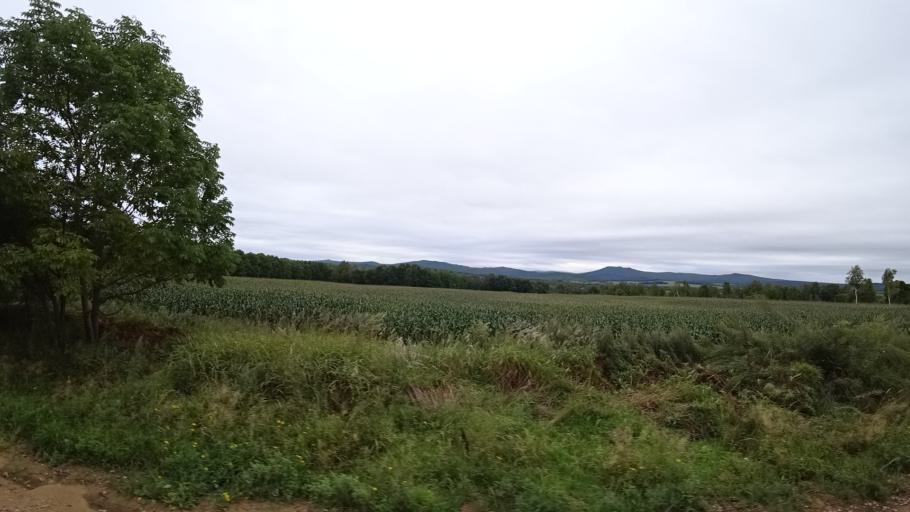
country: RU
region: Primorskiy
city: Rettikhovka
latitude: 44.1562
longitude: 132.6835
